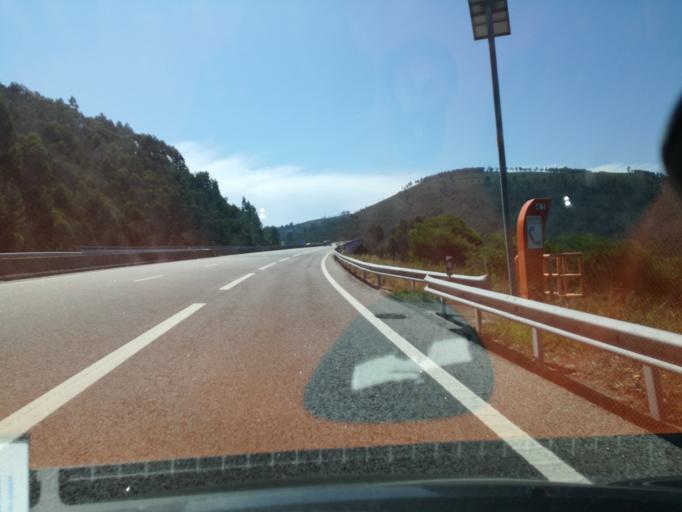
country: PT
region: Viana do Castelo
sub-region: Vila Nova de Cerveira
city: Vila Nova de Cerveira
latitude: 41.8655
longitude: -8.7805
